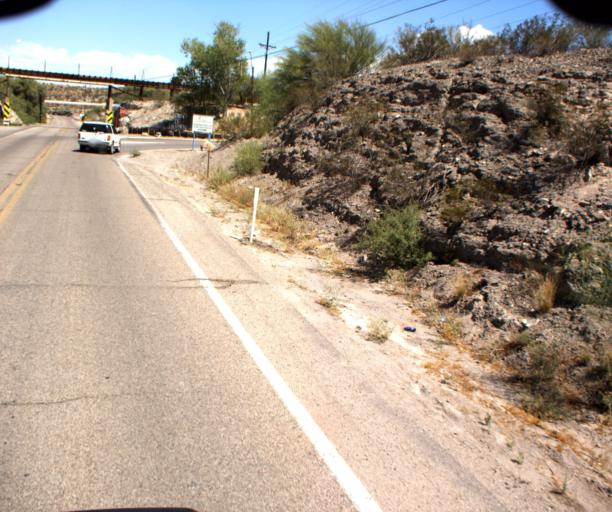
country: US
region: Arizona
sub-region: Pinal County
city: Kearny
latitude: 32.9997
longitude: -110.7876
